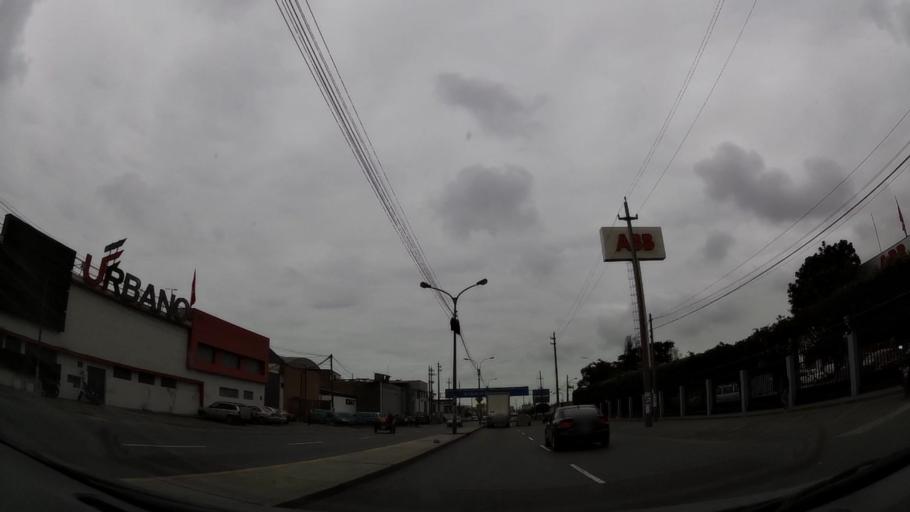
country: PE
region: Callao
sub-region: Callao
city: Callao
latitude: -12.0469
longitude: -77.0809
